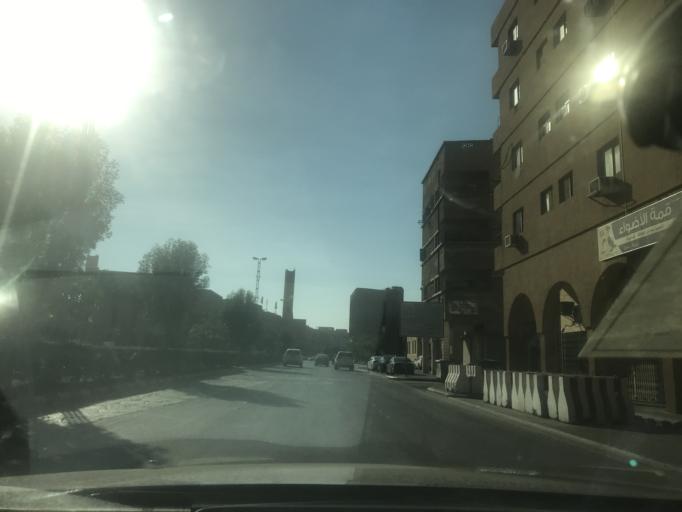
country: SA
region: Ar Riyad
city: Riyadh
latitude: 24.6325
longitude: 46.7134
